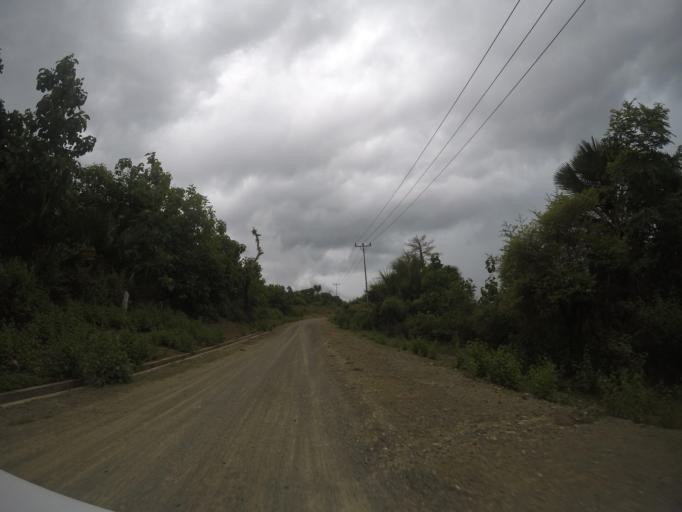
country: TL
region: Bobonaro
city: Maliana
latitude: -8.8494
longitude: 125.0734
